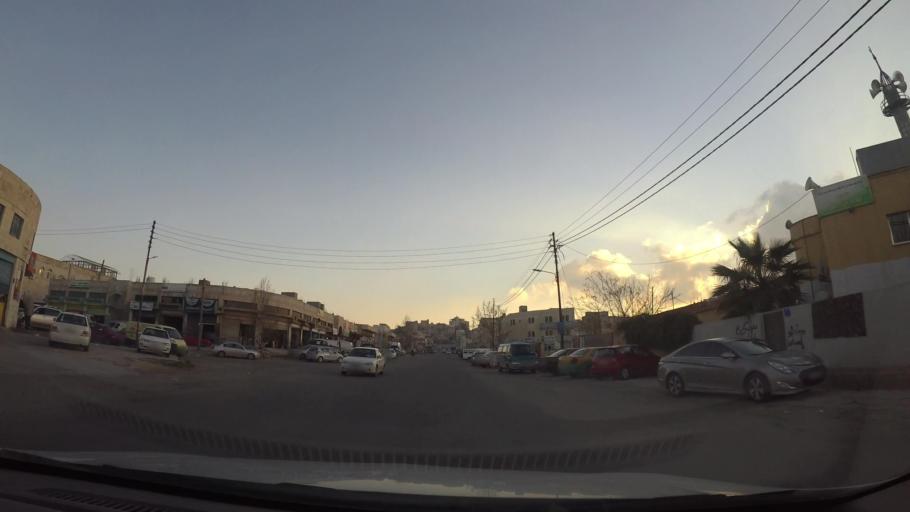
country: JO
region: Amman
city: Al Quwaysimah
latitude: 31.9107
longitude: 35.9204
